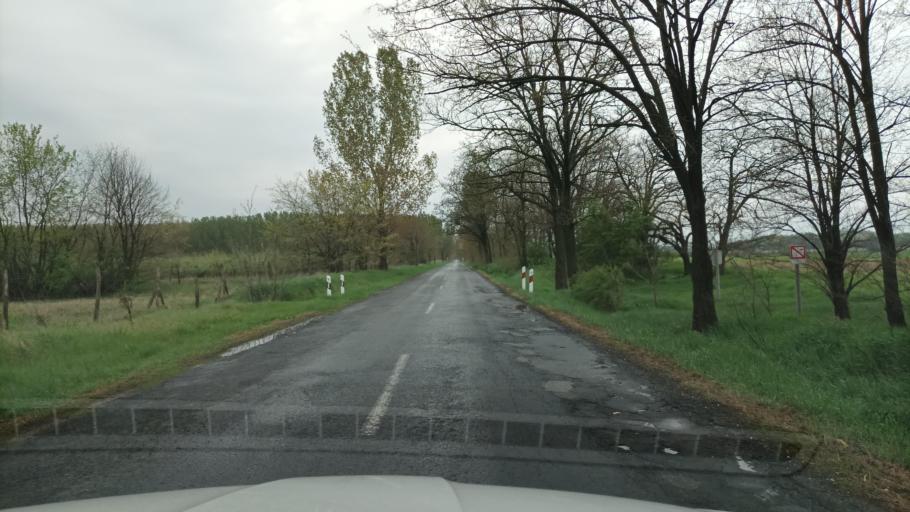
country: HU
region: Pest
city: Danszentmiklos
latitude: 47.2167
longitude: 19.5741
